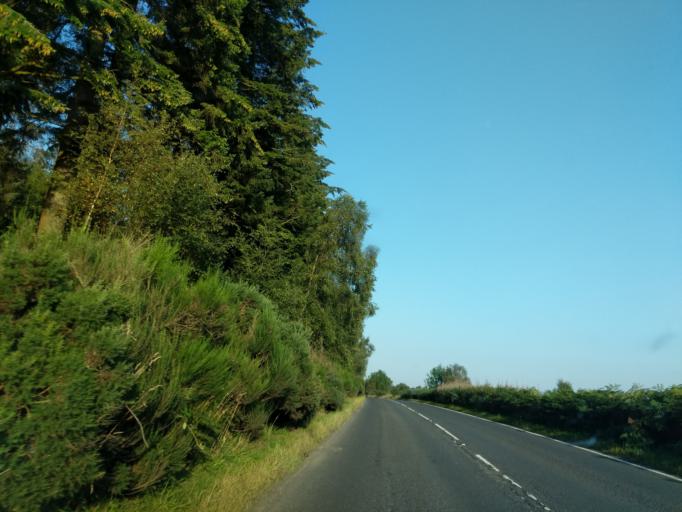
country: GB
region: Scotland
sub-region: Stirling
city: Balfron
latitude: 56.1748
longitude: -4.3433
